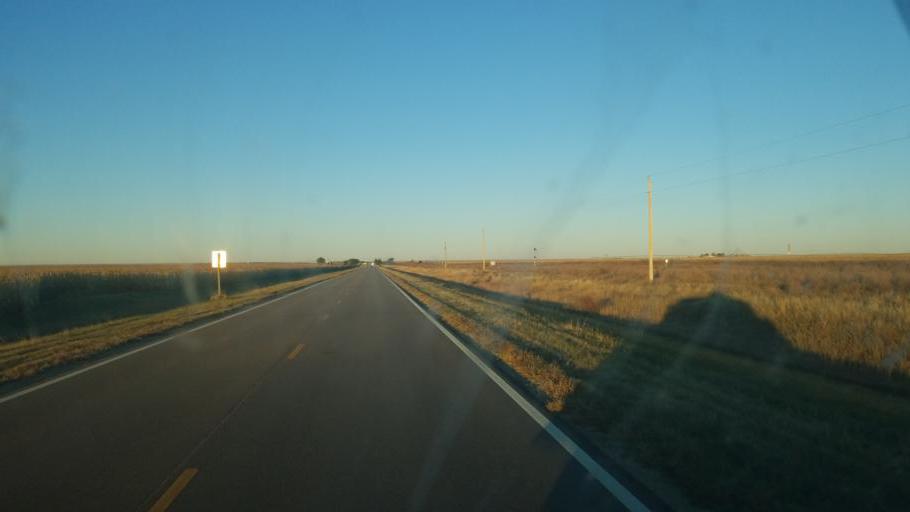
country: US
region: Kansas
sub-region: Wallace County
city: Sharon Springs
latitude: 38.8594
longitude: -102.0322
